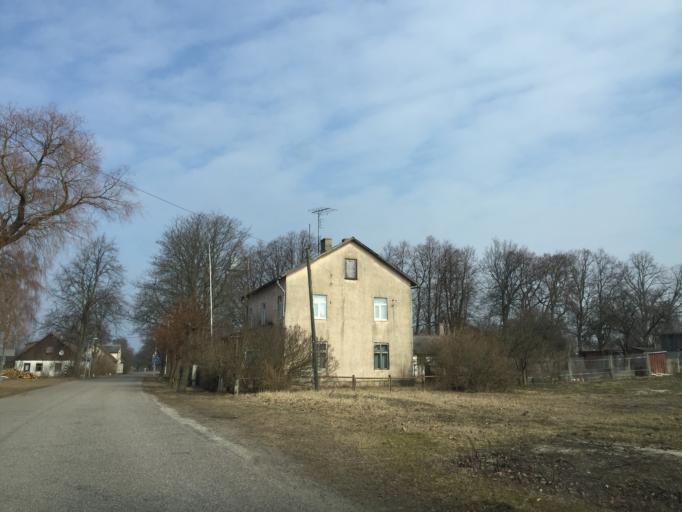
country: LV
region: Salacgrivas
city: Ainazi
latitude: 57.8738
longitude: 24.3610
